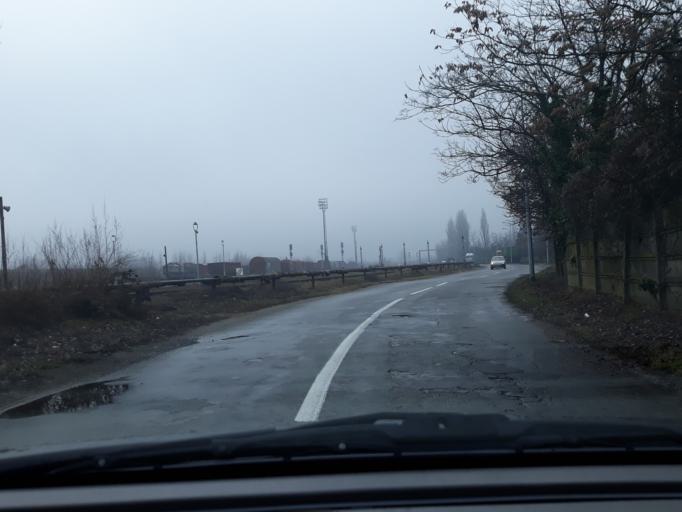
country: RO
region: Bihor
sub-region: Comuna Sanmartin
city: Sanmartin
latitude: 47.0428
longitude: 21.9624
